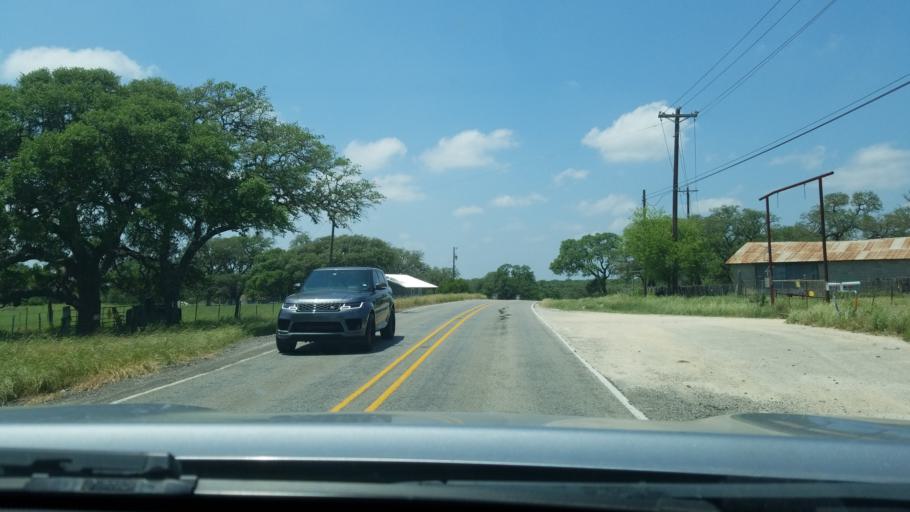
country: US
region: Texas
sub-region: Hays County
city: Woodcreek
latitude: 30.0407
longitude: -98.1907
